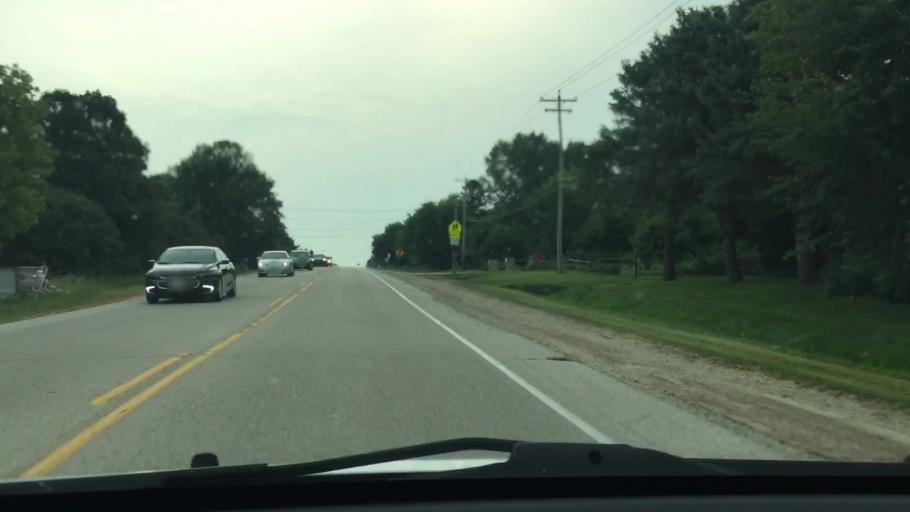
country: US
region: Wisconsin
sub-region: Waukesha County
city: New Berlin
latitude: 42.9908
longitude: -88.1512
